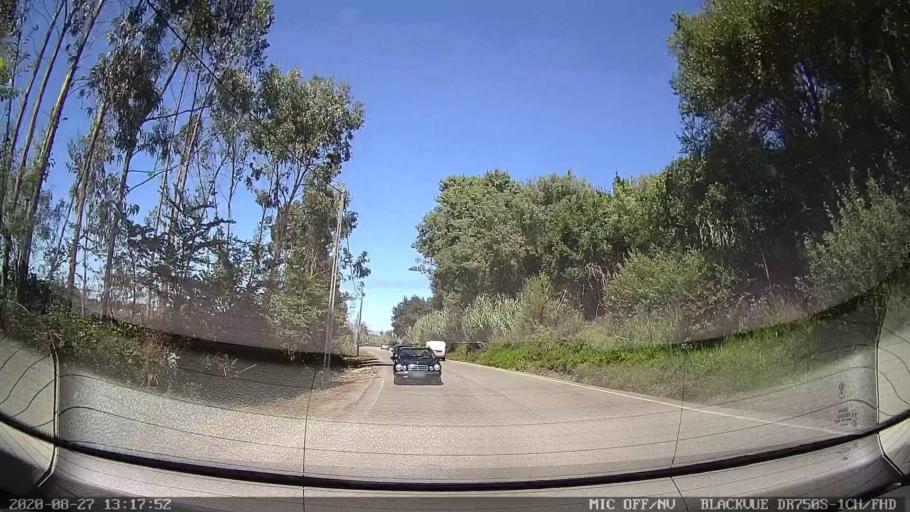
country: PT
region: Aveiro
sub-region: Vagos
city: Vagos
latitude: 40.5784
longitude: -8.6800
